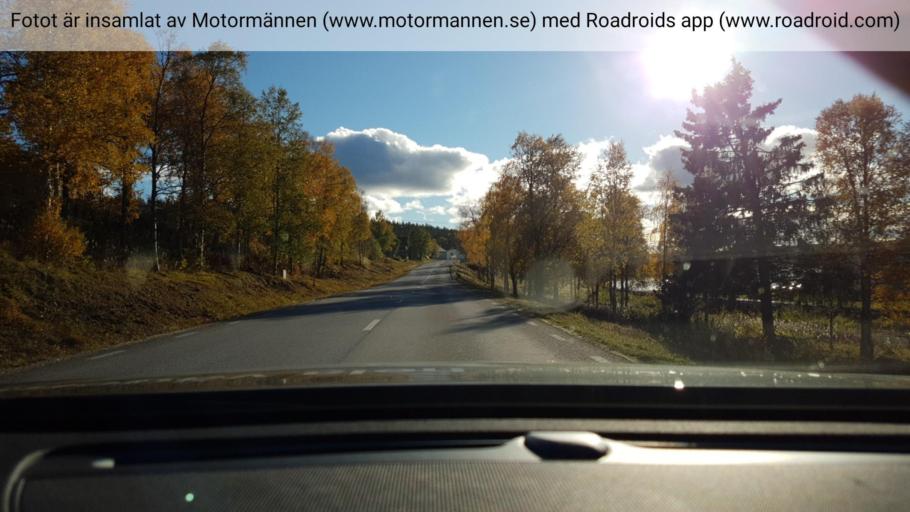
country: SE
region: Norrbotten
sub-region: Jokkmokks Kommun
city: Jokkmokk
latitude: 66.9627
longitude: 19.8257
